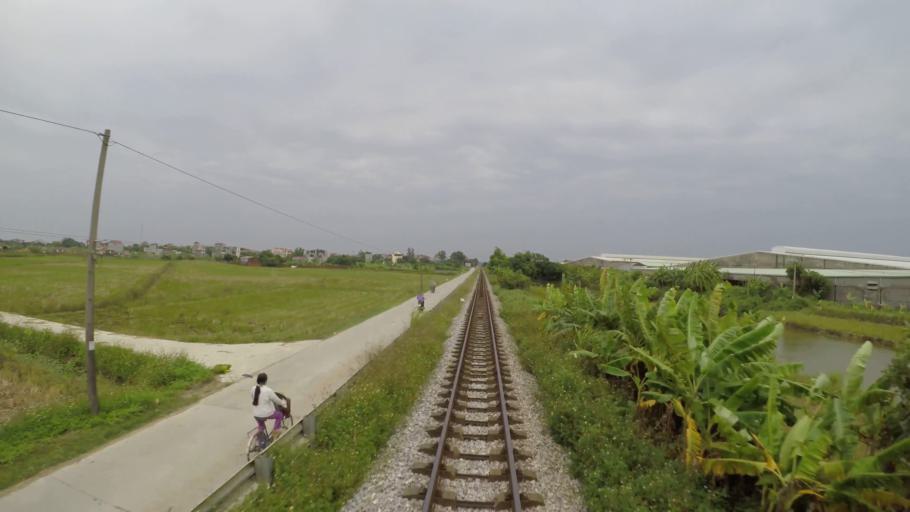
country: VN
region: Hai Duong
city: Lai Cach
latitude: 20.9523
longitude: 106.2318
